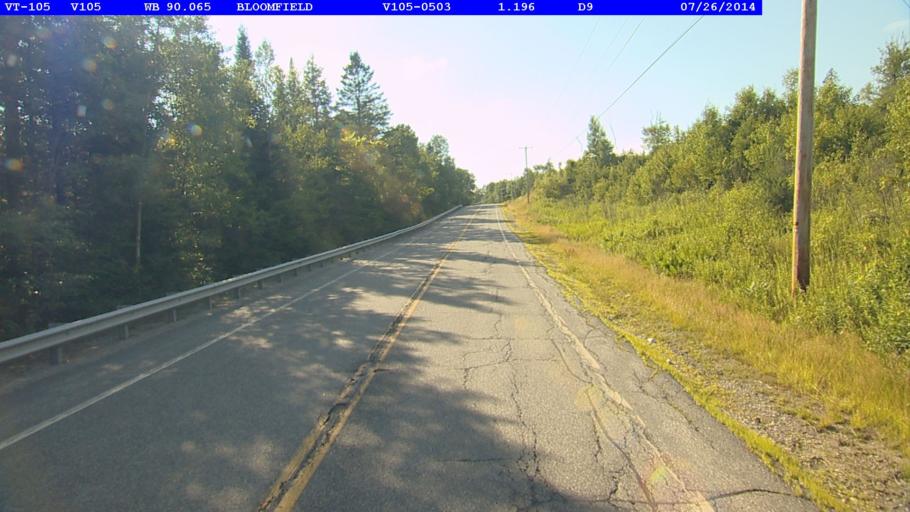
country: US
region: New Hampshire
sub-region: Coos County
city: Stratford
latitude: 44.7782
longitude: -71.6680
